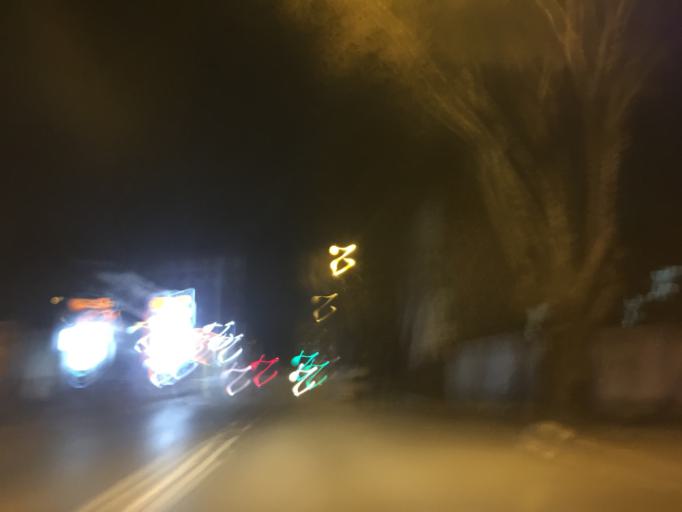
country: TR
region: Istanbul
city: Icmeler
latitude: 40.8188
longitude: 29.3058
